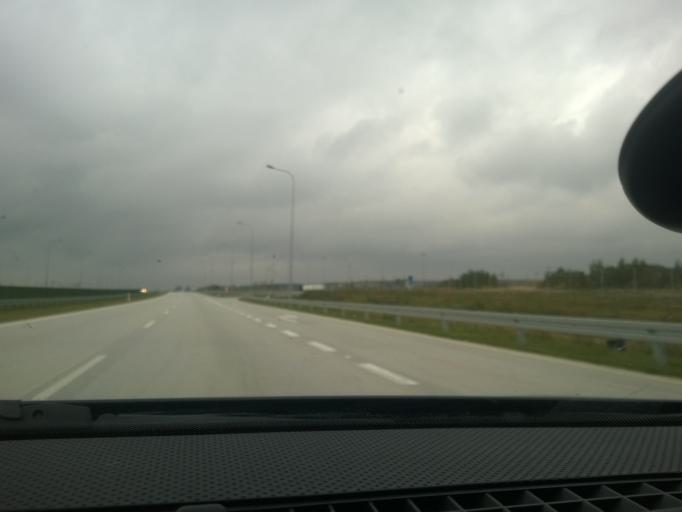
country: PL
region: Lodz Voivodeship
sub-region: Powiat zgierski
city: Strykow
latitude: 51.8405
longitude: 19.6589
